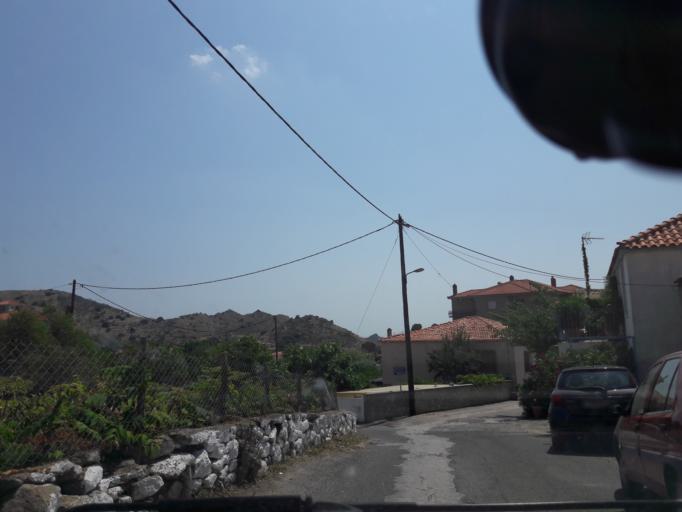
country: GR
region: North Aegean
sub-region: Nomos Lesvou
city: Myrina
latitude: 39.8539
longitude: 25.0868
